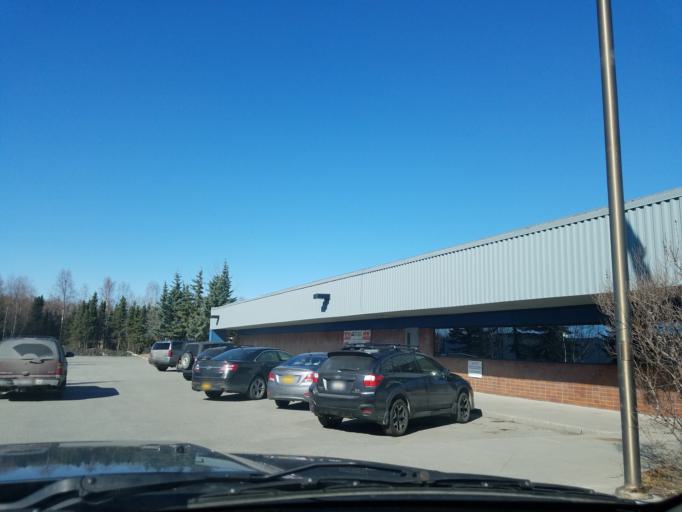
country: US
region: Alaska
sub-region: Anchorage Municipality
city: Elmendorf Air Force Base
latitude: 61.1972
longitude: -149.7353
